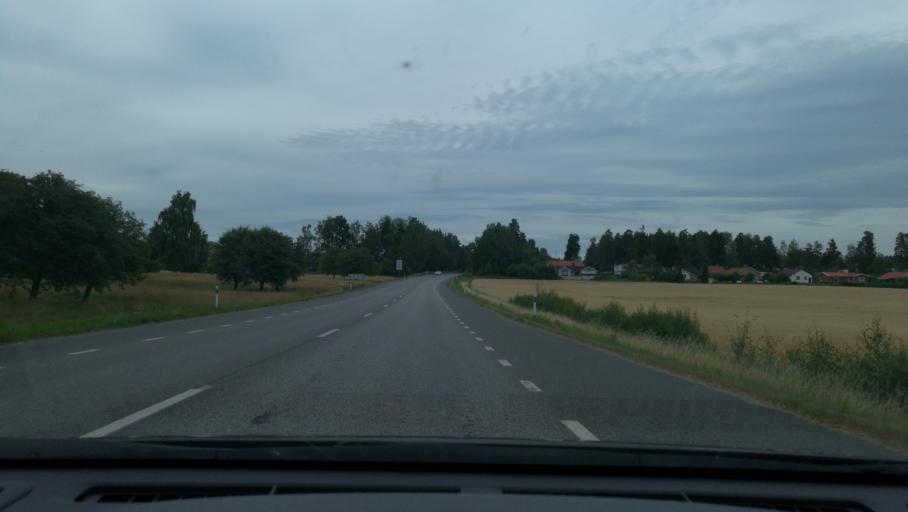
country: SE
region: Soedermanland
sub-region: Katrineholms Kommun
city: Katrineholm
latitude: 58.9819
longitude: 16.2090
